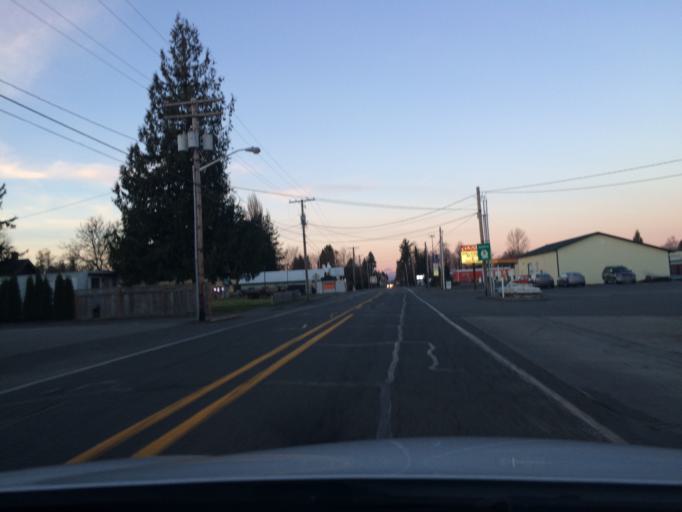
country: US
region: Washington
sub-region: Whatcom County
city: Nooksack
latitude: 48.9204
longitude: -122.3219
